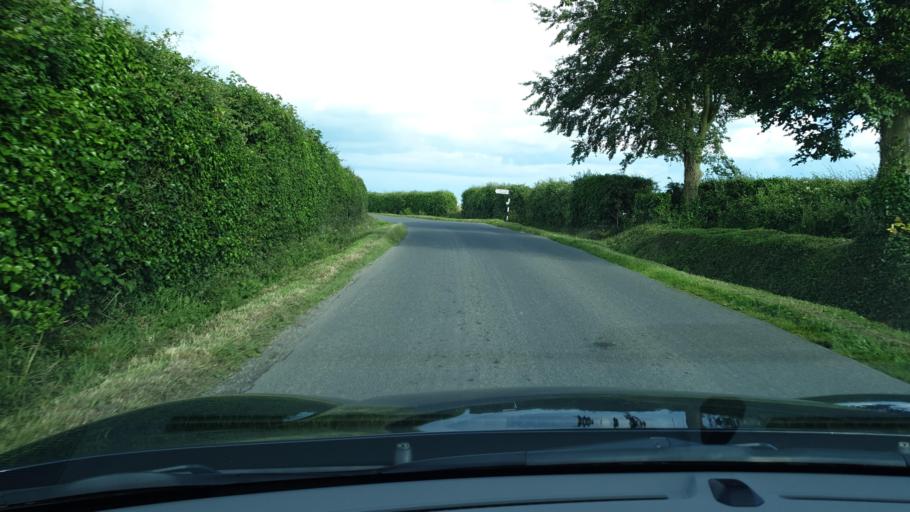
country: IE
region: Leinster
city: Lusk
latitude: 53.5576
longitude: -6.1678
